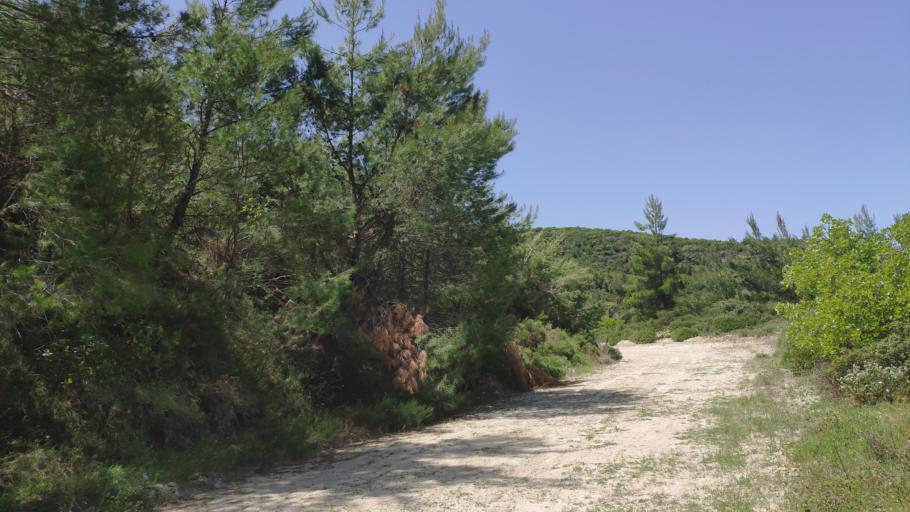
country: GR
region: Attica
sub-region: Nomarchia Anatolikis Attikis
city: Kalamos
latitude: 38.2774
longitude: 23.8489
